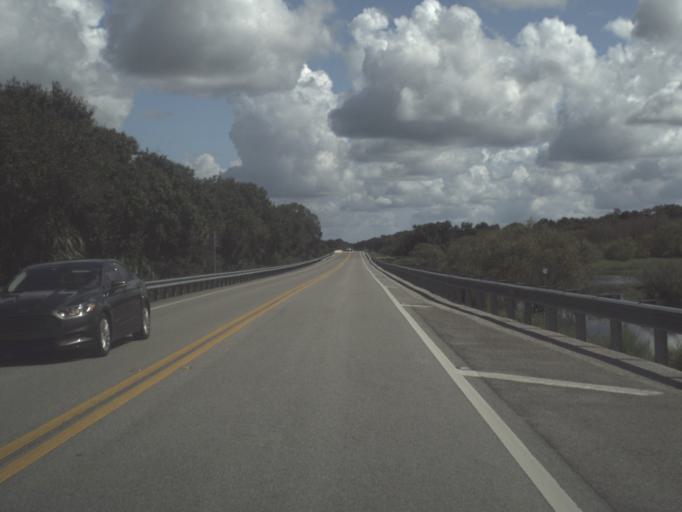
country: US
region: Florida
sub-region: Sarasota County
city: Lake Sarasota
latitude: 27.2376
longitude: -82.3148
